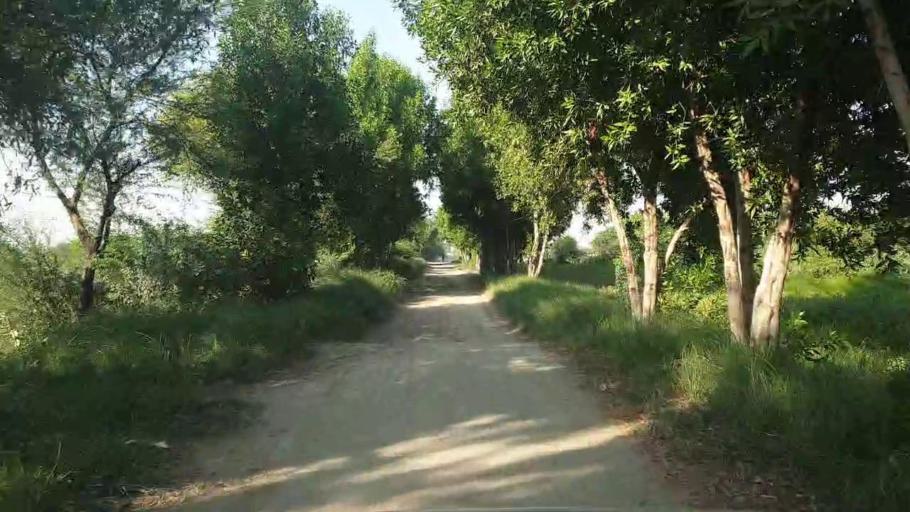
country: PK
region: Sindh
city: Badin
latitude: 24.6275
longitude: 68.8149
